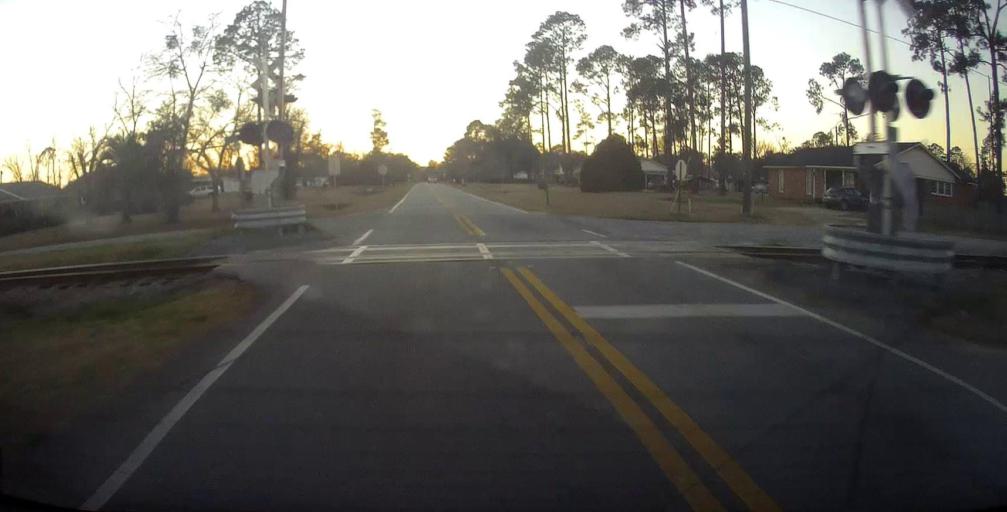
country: US
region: Georgia
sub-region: Dougherty County
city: Albany
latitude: 31.5292
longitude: -84.1234
